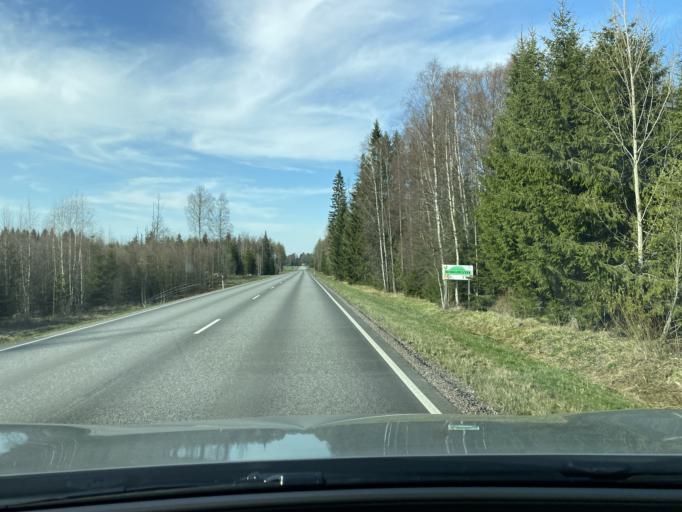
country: FI
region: Haeme
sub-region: Riihimaeki
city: Loppi
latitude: 60.5538
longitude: 24.5218
